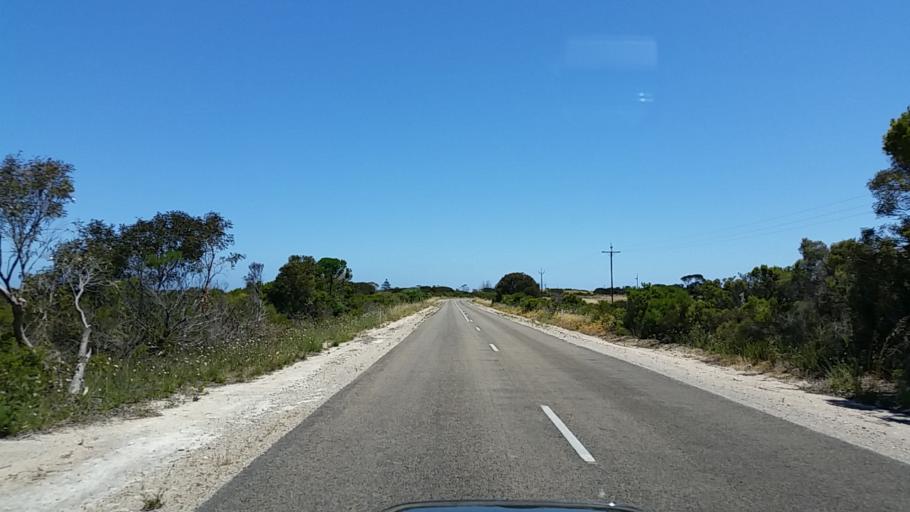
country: AU
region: South Australia
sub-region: Yorke Peninsula
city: Honiton
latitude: -35.2218
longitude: 136.9953
